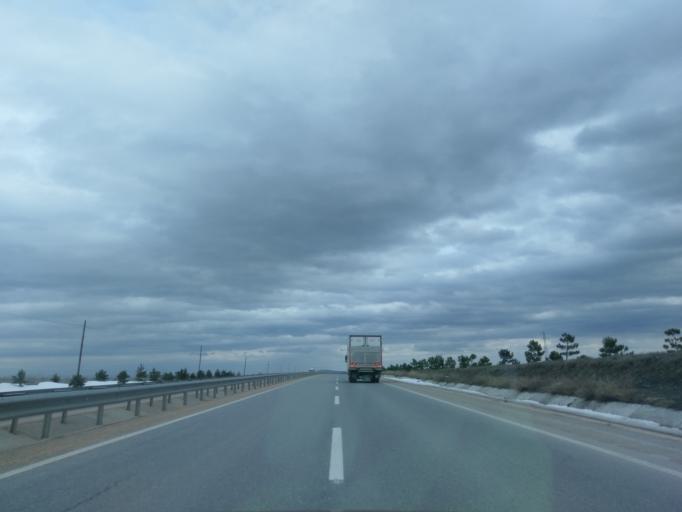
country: TR
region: Eskisehir
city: Inonu
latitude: 39.7243
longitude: 30.2769
